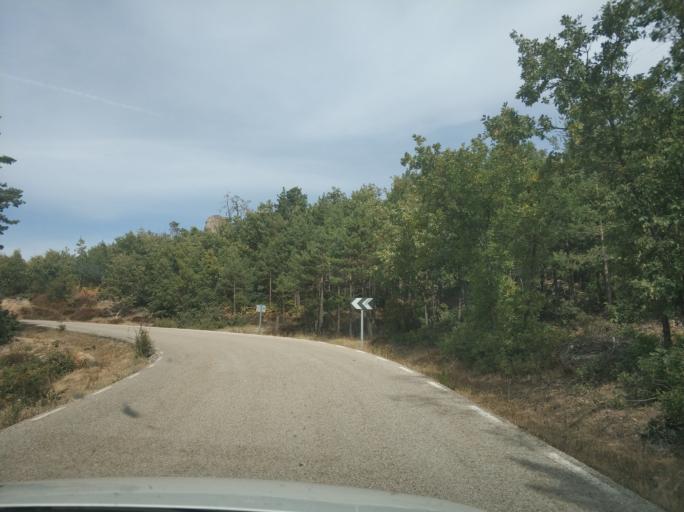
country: ES
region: Castille and Leon
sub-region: Provincia de Soria
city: Duruelo de la Sierra
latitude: 41.9077
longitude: -2.9445
